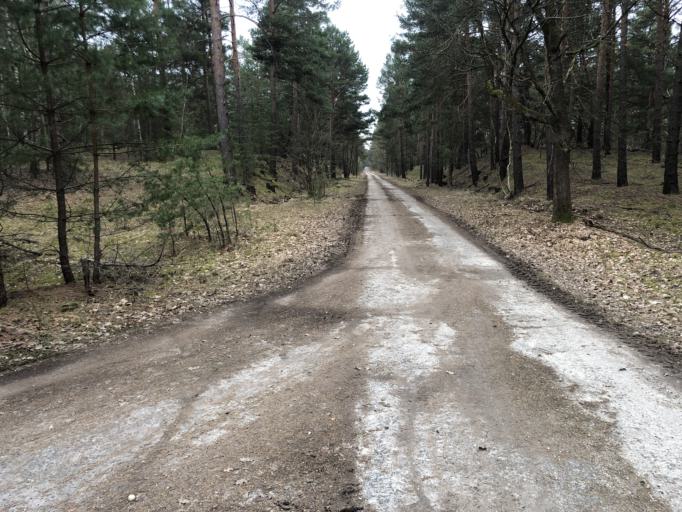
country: DE
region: Brandenburg
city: Zossen
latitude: 52.1452
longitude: 13.5177
